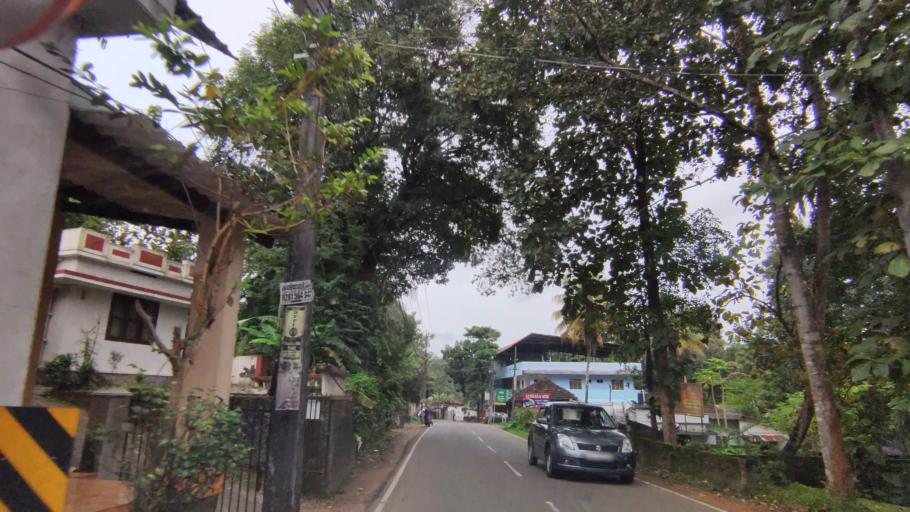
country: IN
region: Kerala
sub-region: Kottayam
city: Kottayam
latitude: 9.6528
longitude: 76.5238
